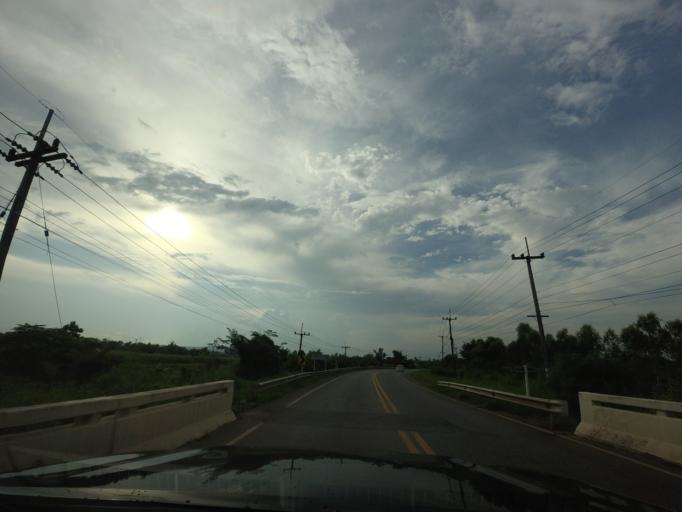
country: TH
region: Changwat Udon Thani
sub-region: Amphoe Ban Phue
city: Ban Phue
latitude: 17.7132
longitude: 102.4130
